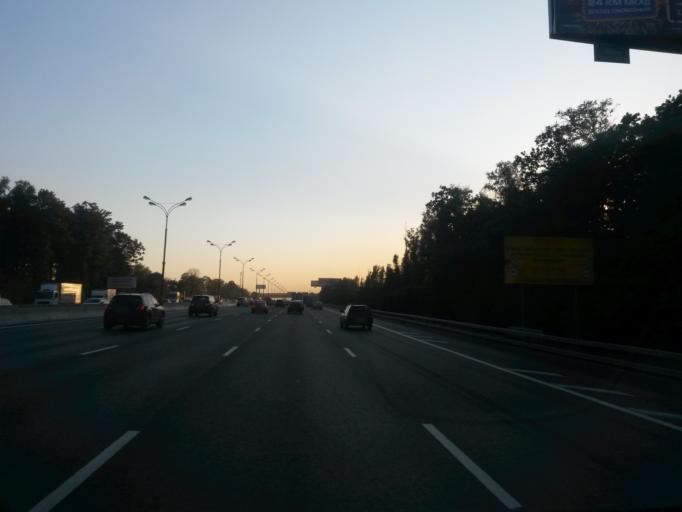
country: RU
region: Moskovskaya
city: Razvilka
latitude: 55.6012
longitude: 37.7515
